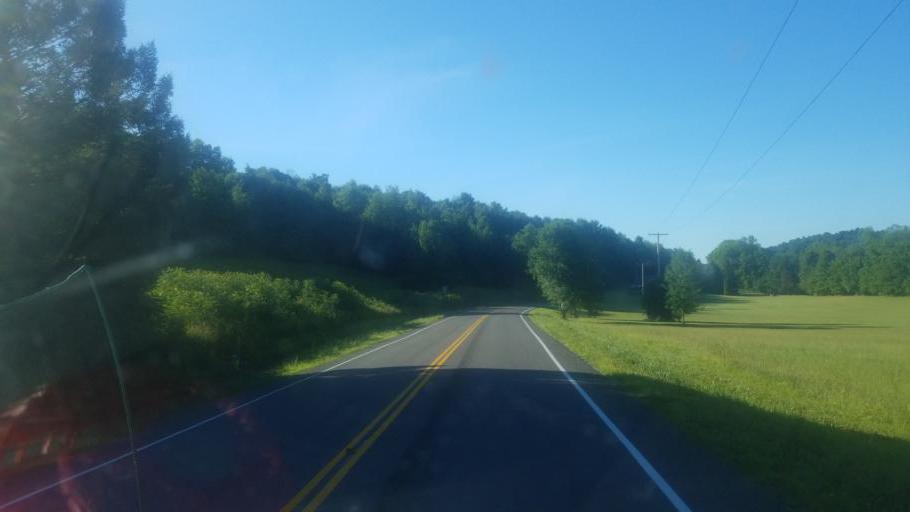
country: US
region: New York
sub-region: Wayne County
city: Lyons
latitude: 43.0864
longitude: -77.0360
